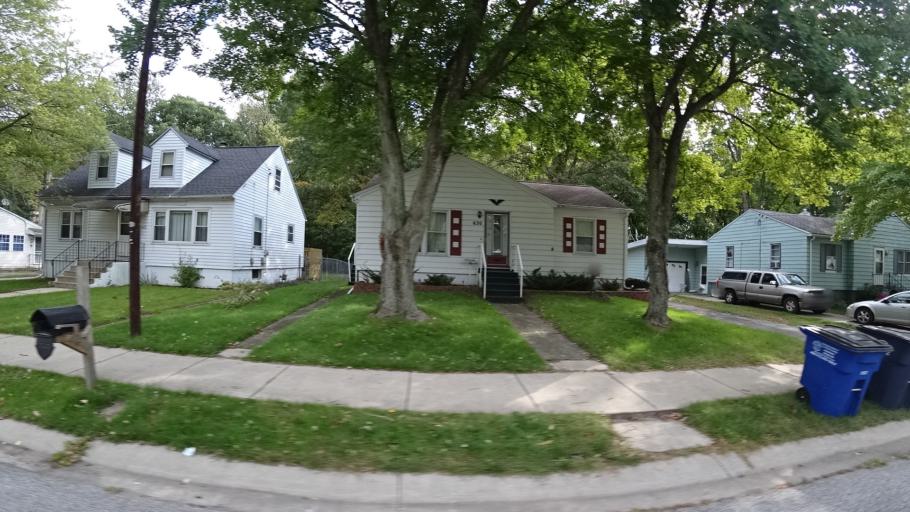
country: US
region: Indiana
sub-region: LaPorte County
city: Trail Creek
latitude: 41.6958
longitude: -86.8665
